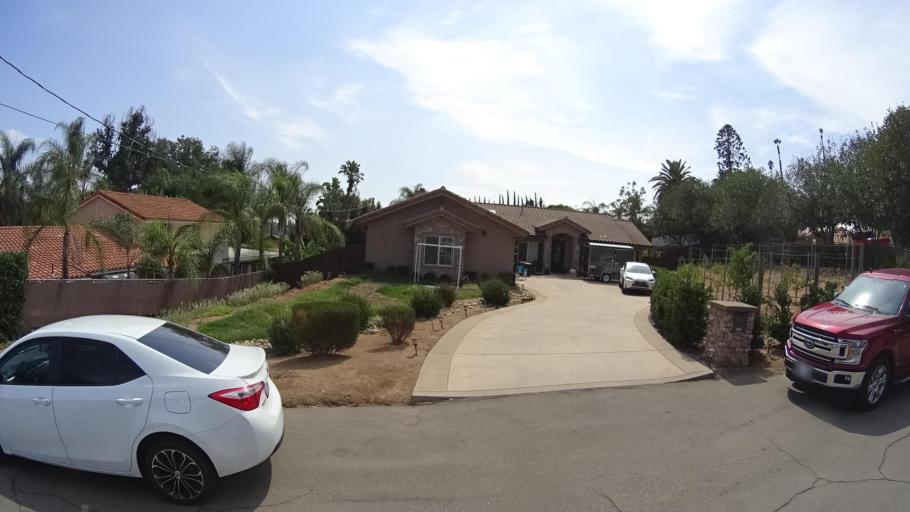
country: US
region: California
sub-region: San Diego County
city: Escondido
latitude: 33.1202
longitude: -117.0493
